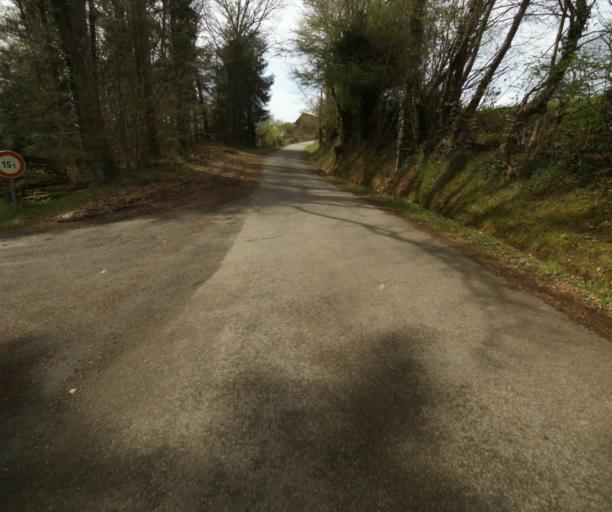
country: FR
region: Limousin
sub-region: Departement de la Correze
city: Laguenne
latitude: 45.2350
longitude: 1.8394
